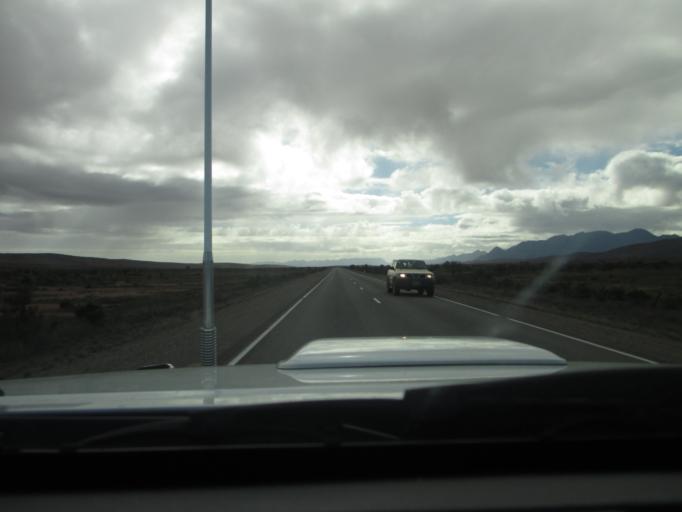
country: AU
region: South Australia
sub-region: Flinders Ranges
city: Quorn
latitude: -31.6214
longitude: 138.3931
